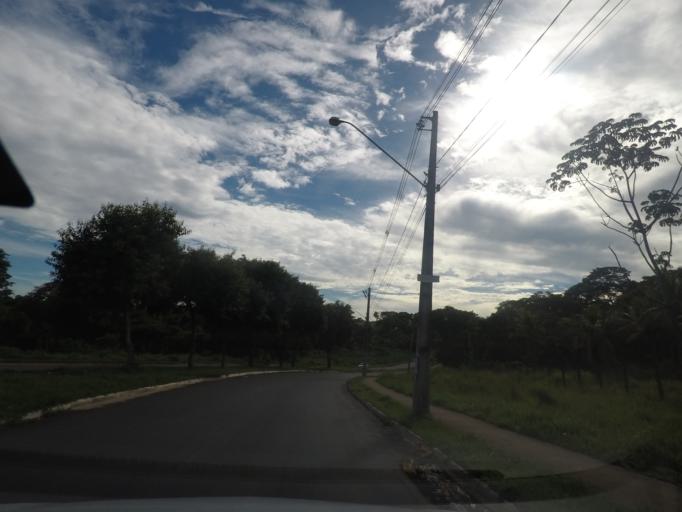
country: BR
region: Goias
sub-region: Aparecida De Goiania
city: Aparecida de Goiania
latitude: -16.8181
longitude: -49.3044
